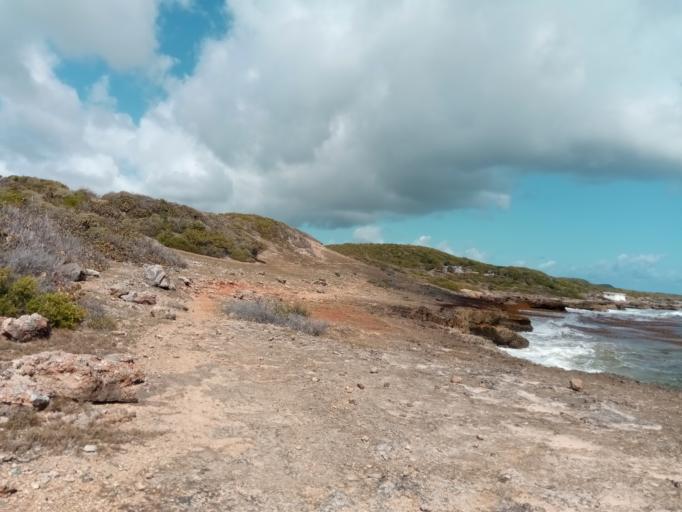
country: GP
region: Guadeloupe
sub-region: Guadeloupe
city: Saint-Francois
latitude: 16.2757
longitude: -61.2445
